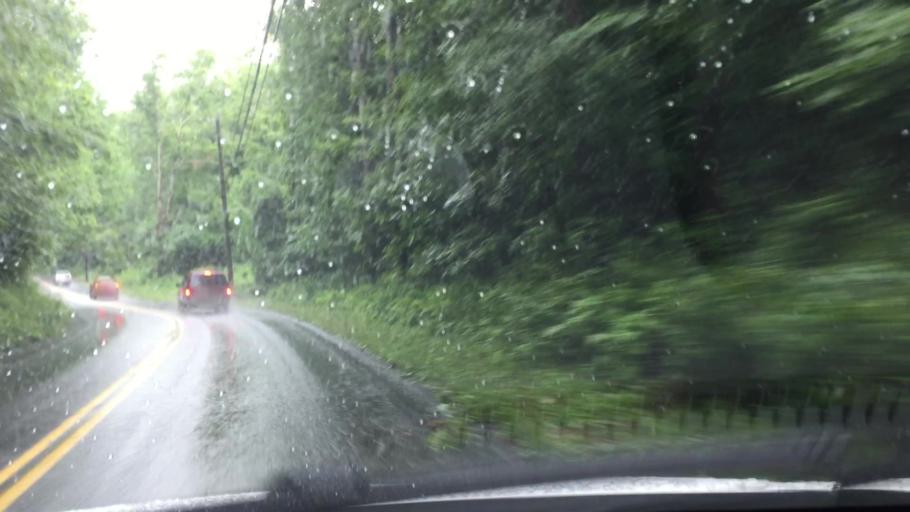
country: US
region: Massachusetts
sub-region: Berkshire County
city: Lanesborough
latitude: 42.5428
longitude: -73.2368
